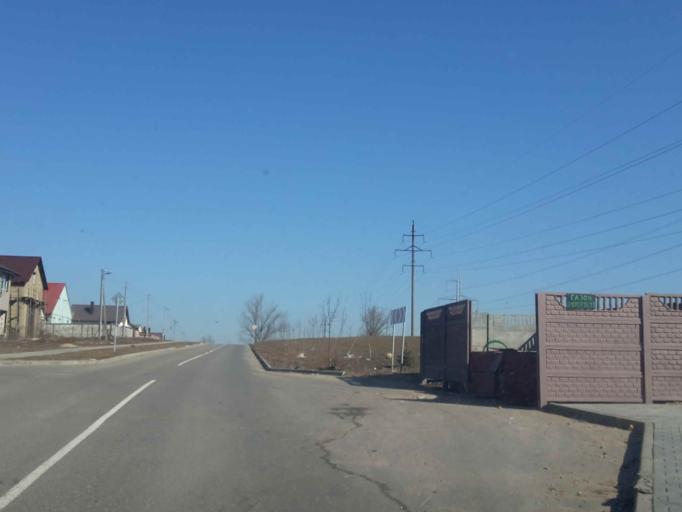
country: BY
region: Minsk
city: Zhdanovichy
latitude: 53.9200
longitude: 27.4119
